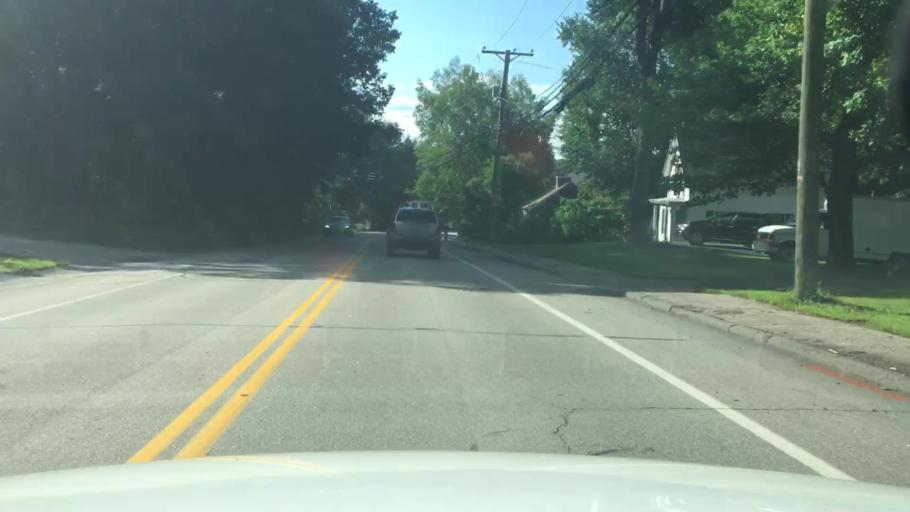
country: US
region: New Hampshire
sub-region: Strafford County
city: Dover
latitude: 43.1748
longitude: -70.8752
